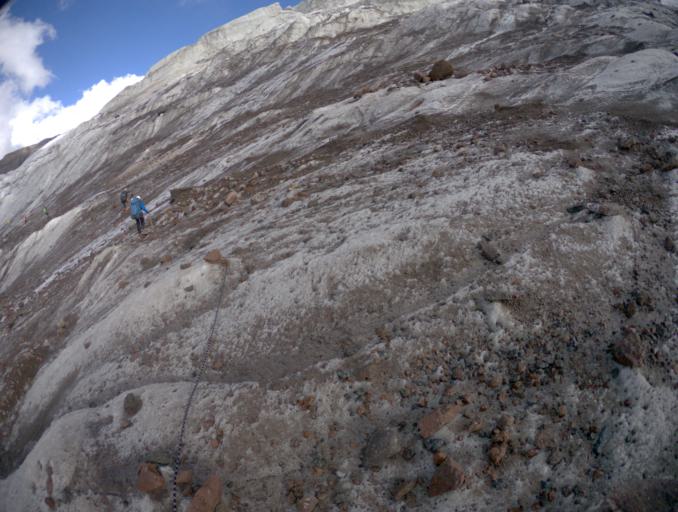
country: RU
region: Kabardino-Balkariya
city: Terskol
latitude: 43.3845
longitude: 42.4206
